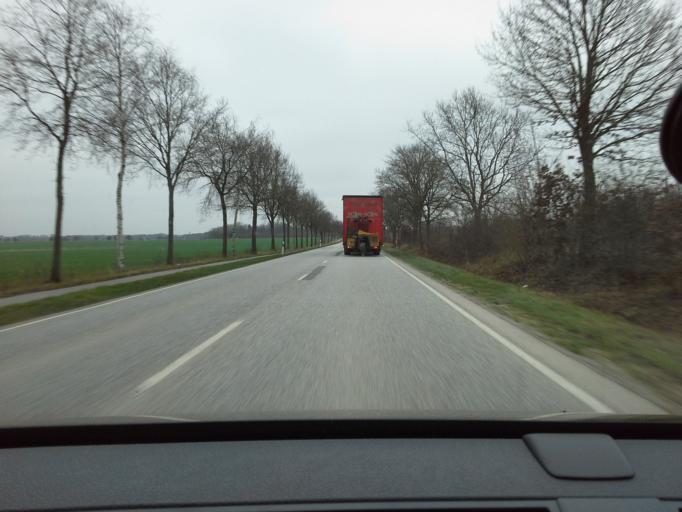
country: DE
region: Schleswig-Holstein
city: Lentfohrden
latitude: 53.8509
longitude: 9.8877
